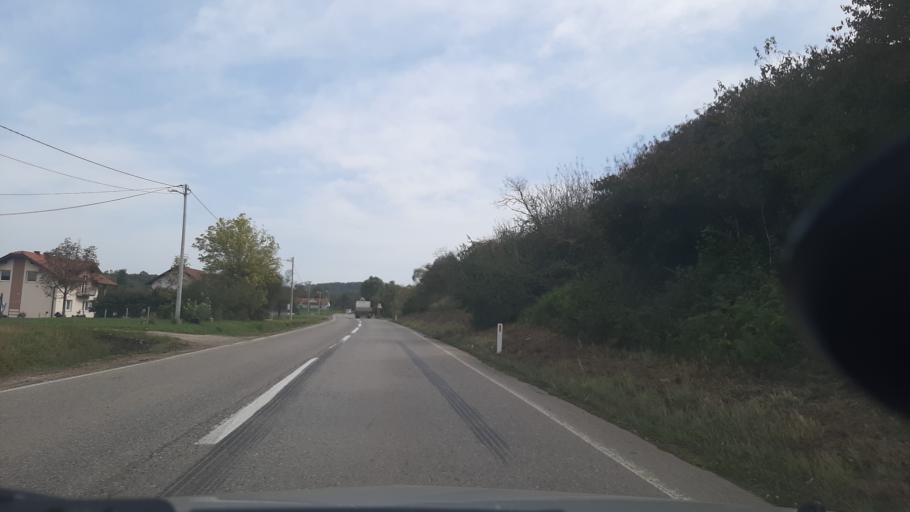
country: BA
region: Republika Srpska
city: Maglajani
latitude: 44.8666
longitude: 17.4199
